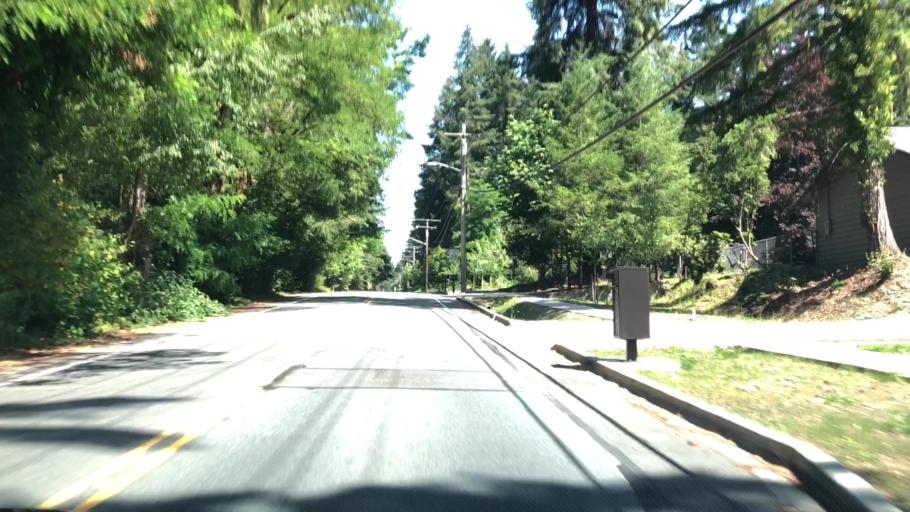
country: US
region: Washington
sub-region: King County
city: Cottage Lake
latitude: 47.7622
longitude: -122.1156
